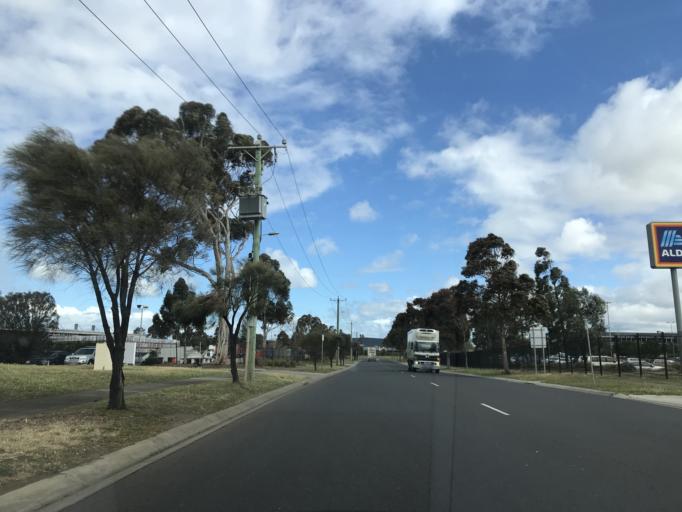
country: AU
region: Victoria
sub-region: Brimbank
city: Derrimut
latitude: -37.8027
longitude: 144.7795
